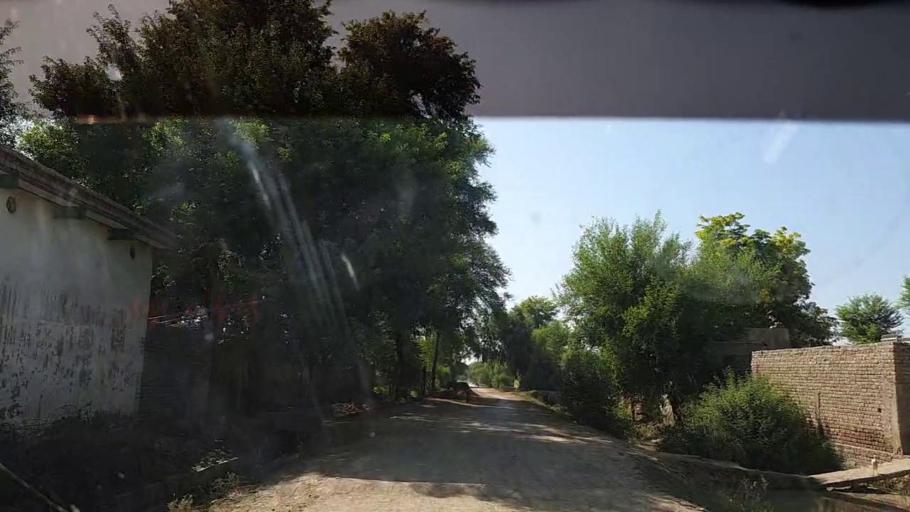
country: PK
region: Sindh
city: Ghauspur
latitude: 28.1726
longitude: 69.0571
